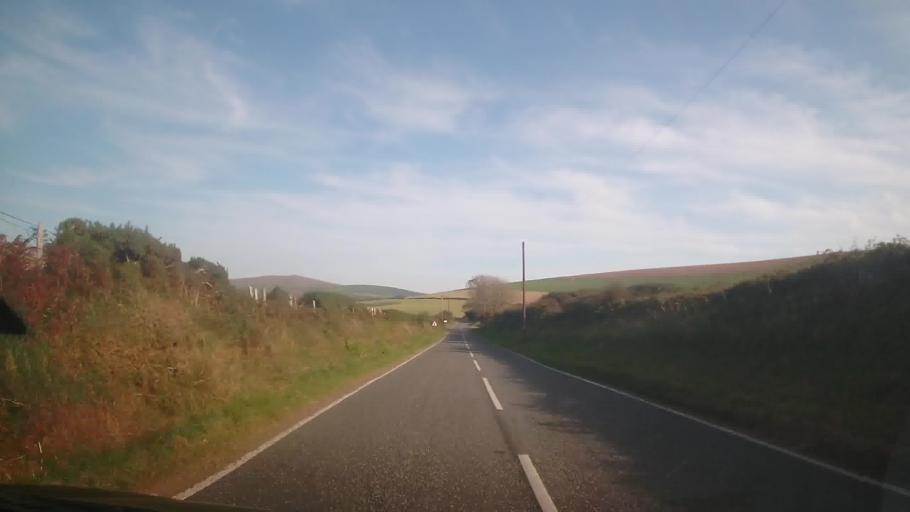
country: GB
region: Wales
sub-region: Pembrokeshire
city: Ambleston
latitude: 51.9662
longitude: -4.9003
